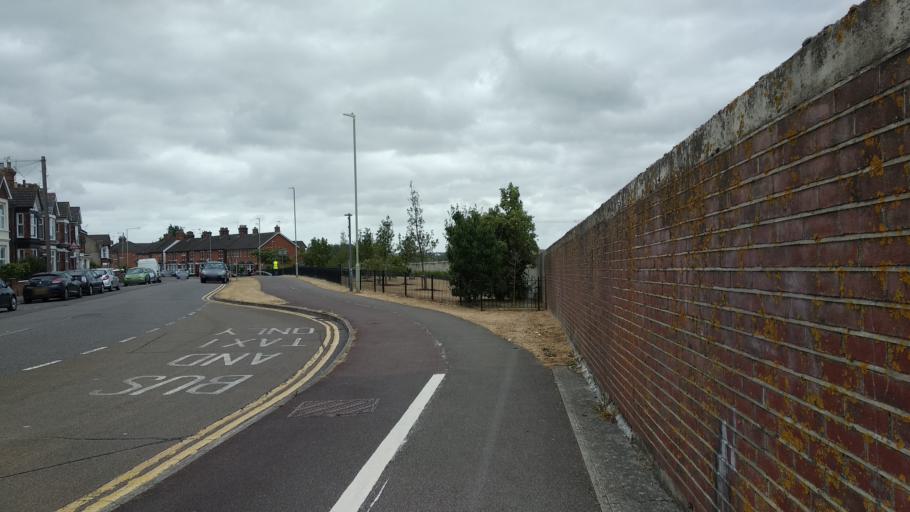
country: GB
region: England
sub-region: Kent
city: Ashford
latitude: 51.1508
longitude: 0.8606
